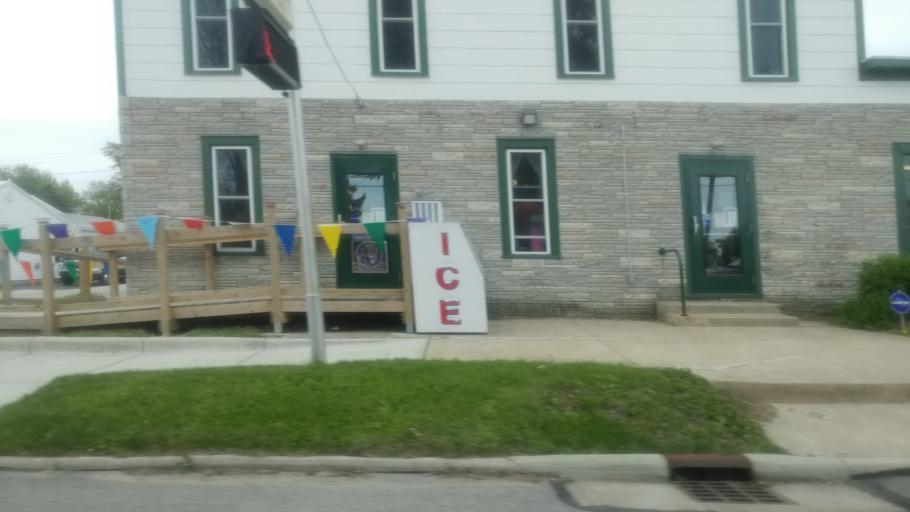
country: US
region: Ohio
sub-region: Sandusky County
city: Gibsonburg
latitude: 41.3412
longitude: -83.2927
